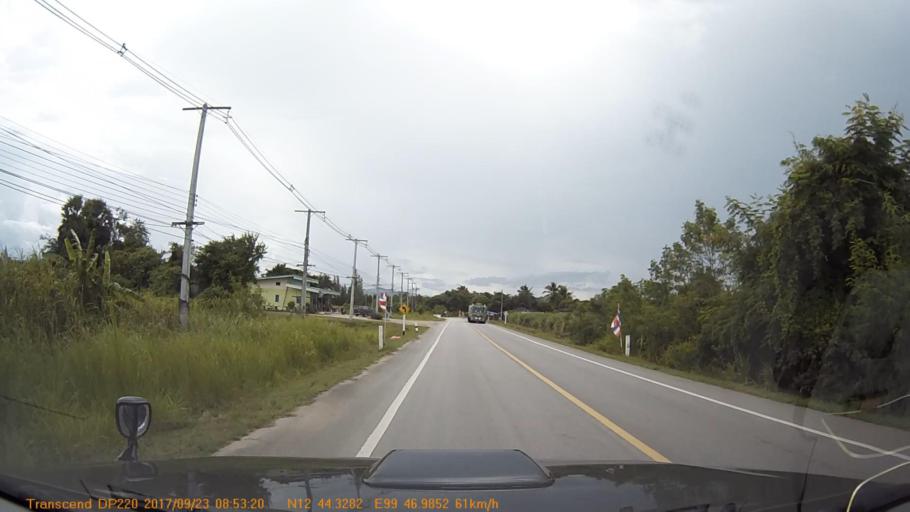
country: TH
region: Phetchaburi
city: Cha-am
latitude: 12.7388
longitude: 99.7830
